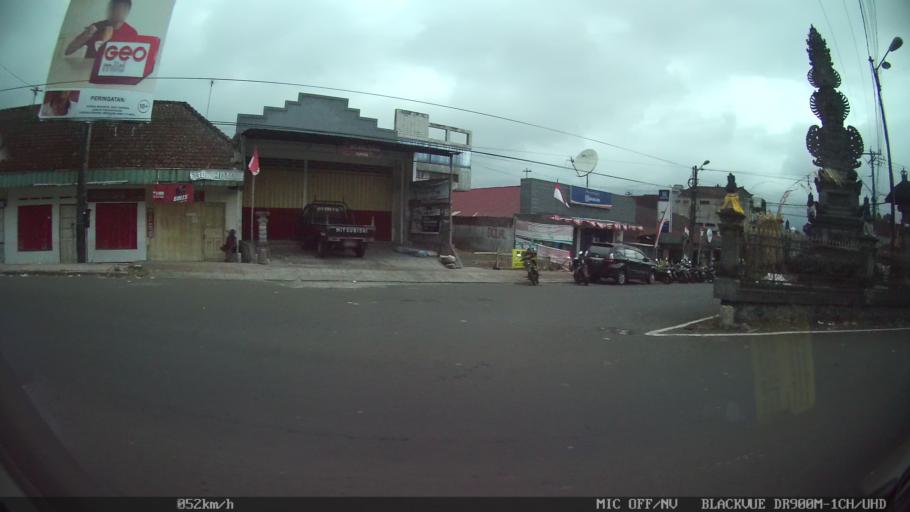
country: ID
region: Bali
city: Bantiran
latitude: -8.3179
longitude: 115.0070
